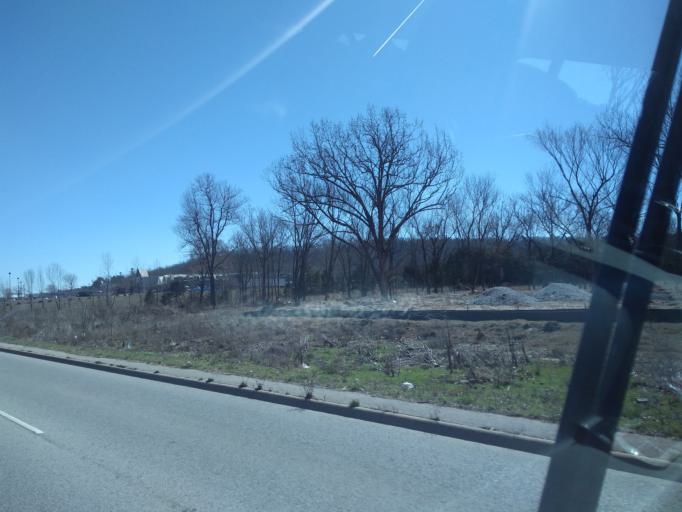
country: US
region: Arkansas
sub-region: Washington County
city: Farmington
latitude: 36.0502
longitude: -94.2098
